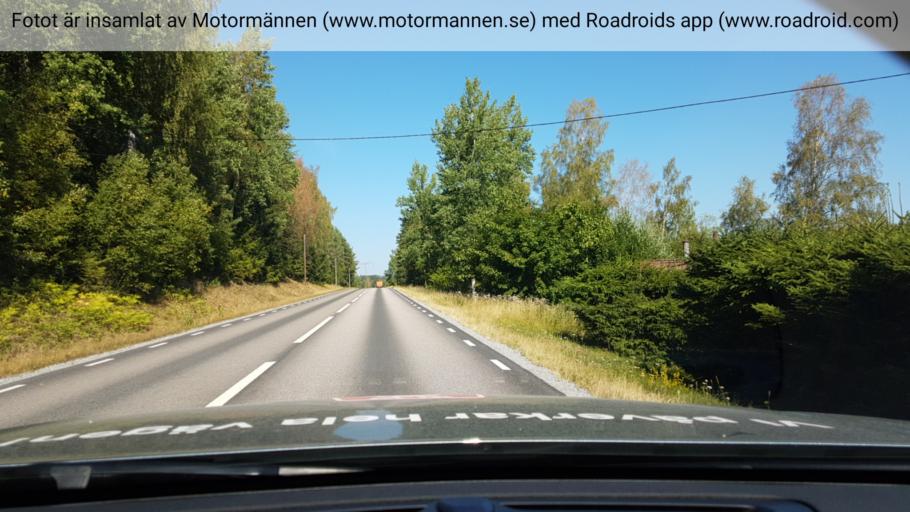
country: SE
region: Stockholm
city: Stenhamra
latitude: 59.3666
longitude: 17.6120
